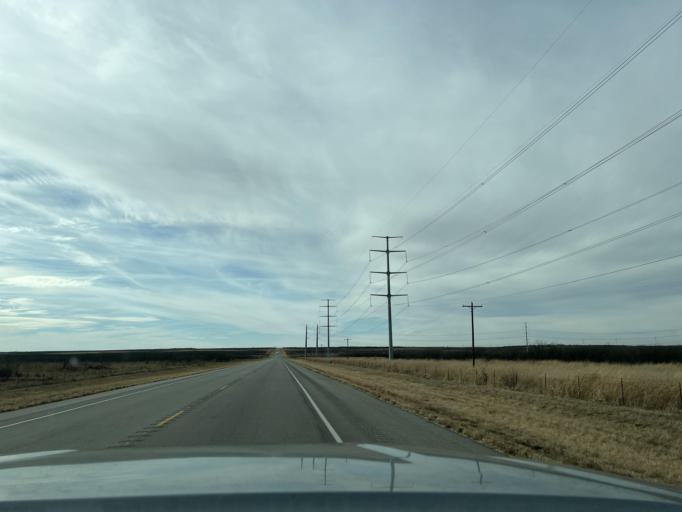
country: US
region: Texas
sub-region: Jones County
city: Anson
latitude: 32.7504
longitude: -99.6463
